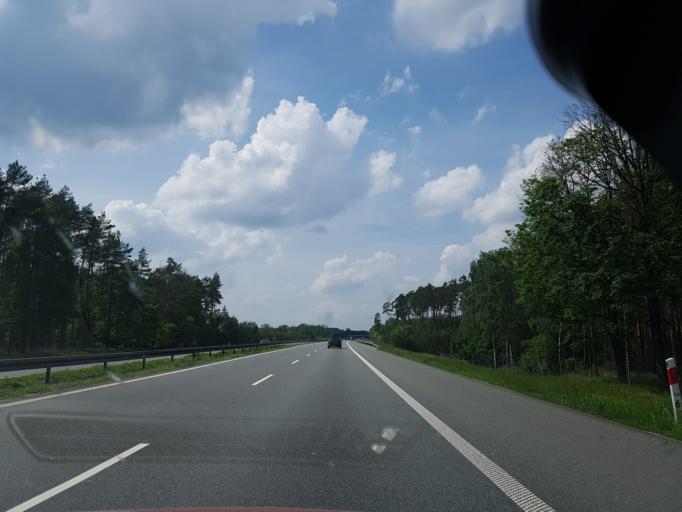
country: PL
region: Opole Voivodeship
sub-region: Powiat opolski
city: Komprachcice
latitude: 50.5873
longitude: 17.8168
